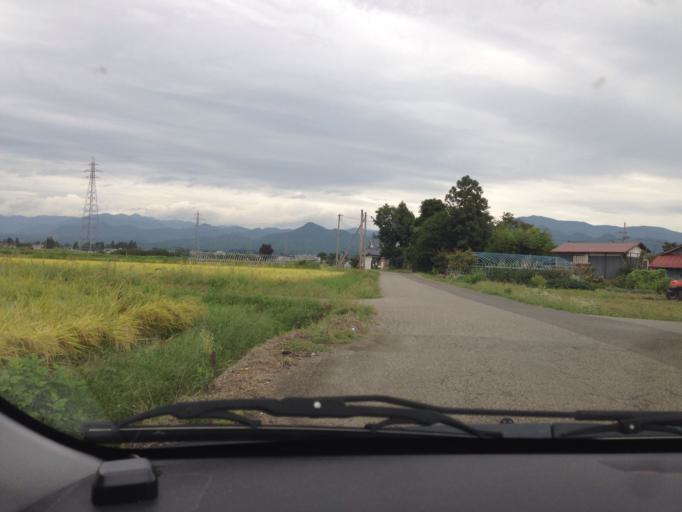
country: JP
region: Fukushima
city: Kitakata
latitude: 37.6325
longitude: 139.8996
